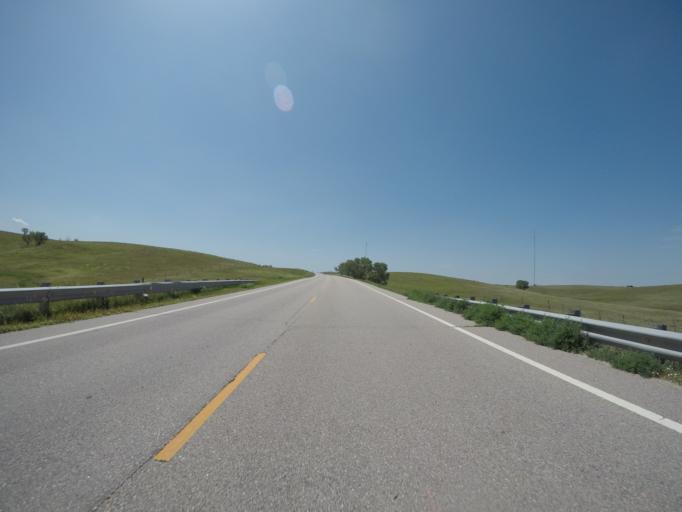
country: US
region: Kansas
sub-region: Osborne County
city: Osborne
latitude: 39.4869
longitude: -98.6965
